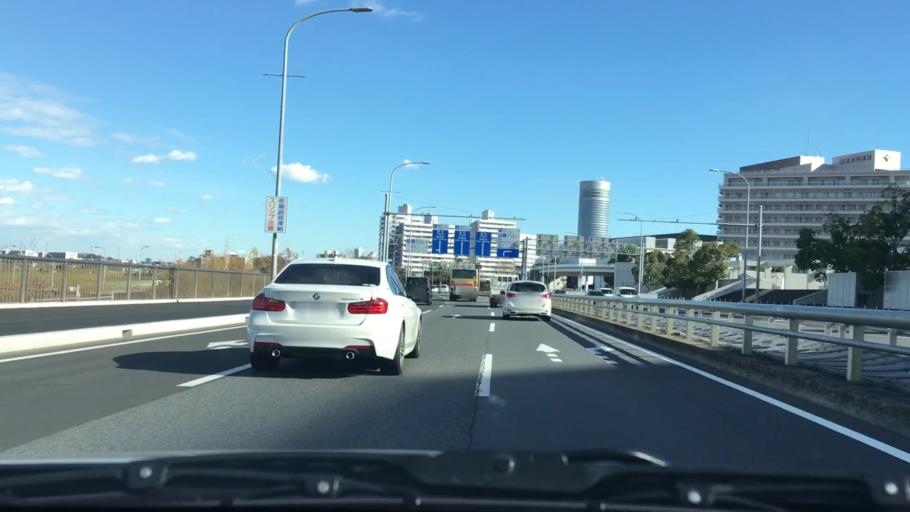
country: JP
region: Kanagawa
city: Yokohama
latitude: 35.5118
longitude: 139.6067
